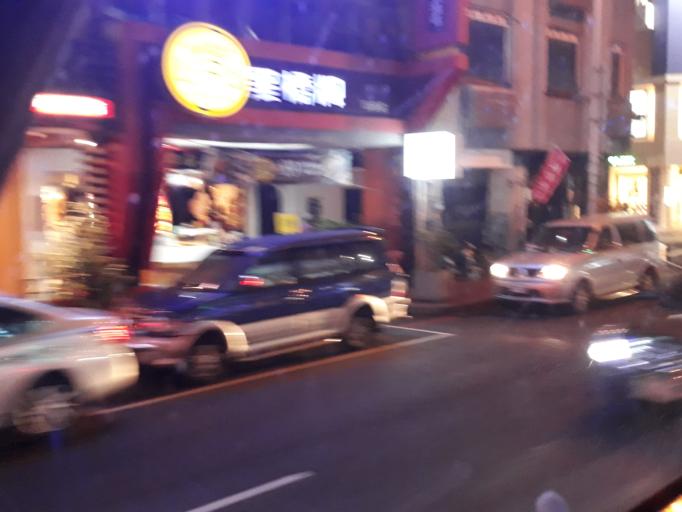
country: TW
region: Taiwan
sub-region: Taichung City
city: Taichung
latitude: 24.1395
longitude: 120.6817
